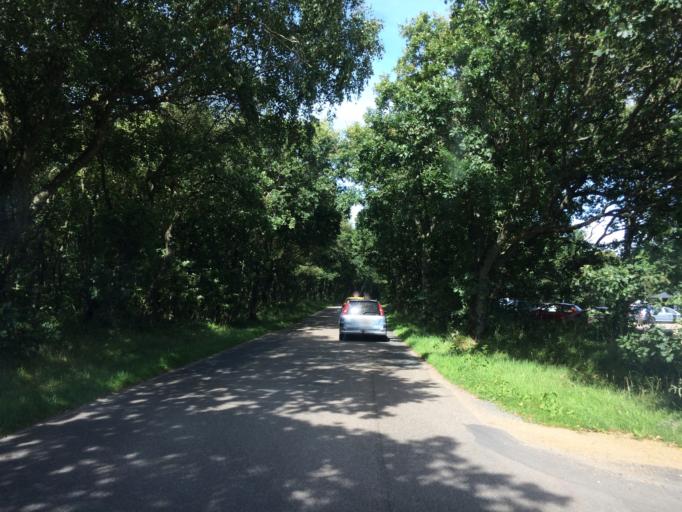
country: DK
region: South Denmark
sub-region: Varde Kommune
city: Oksbol
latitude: 55.6952
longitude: 8.1928
